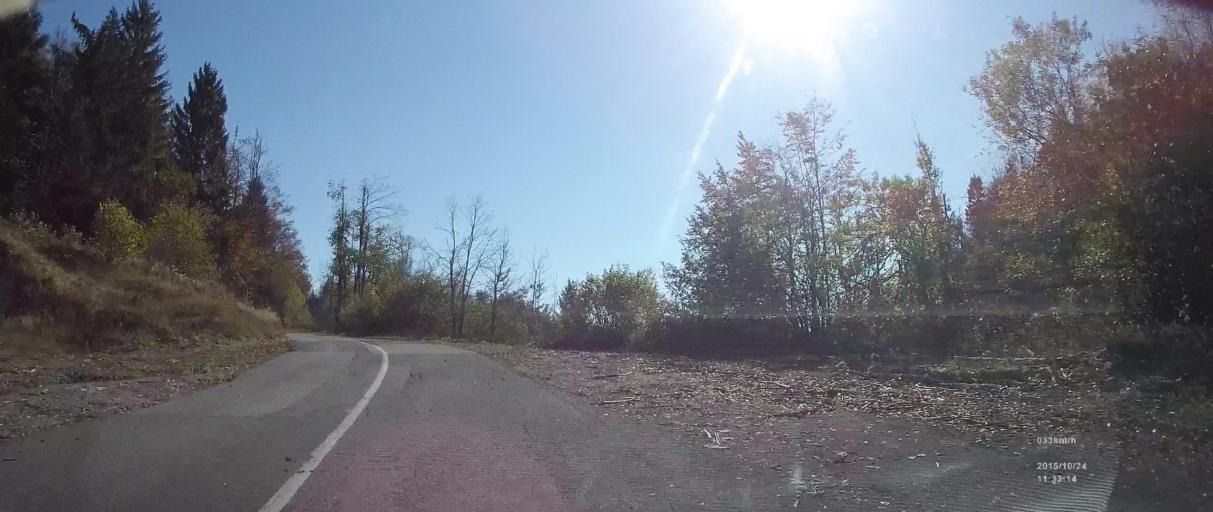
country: HR
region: Primorsko-Goranska
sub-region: Grad Delnice
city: Delnice
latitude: 45.3930
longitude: 14.6849
